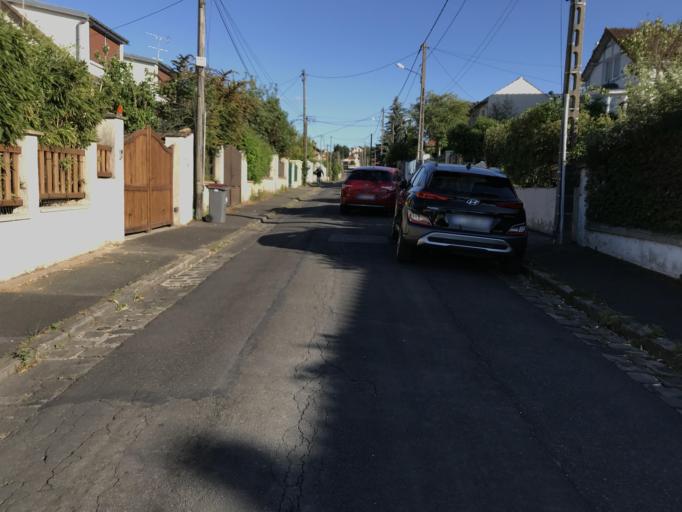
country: FR
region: Ile-de-France
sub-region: Departement de l'Essonne
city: Igny
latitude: 48.7301
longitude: 2.2336
